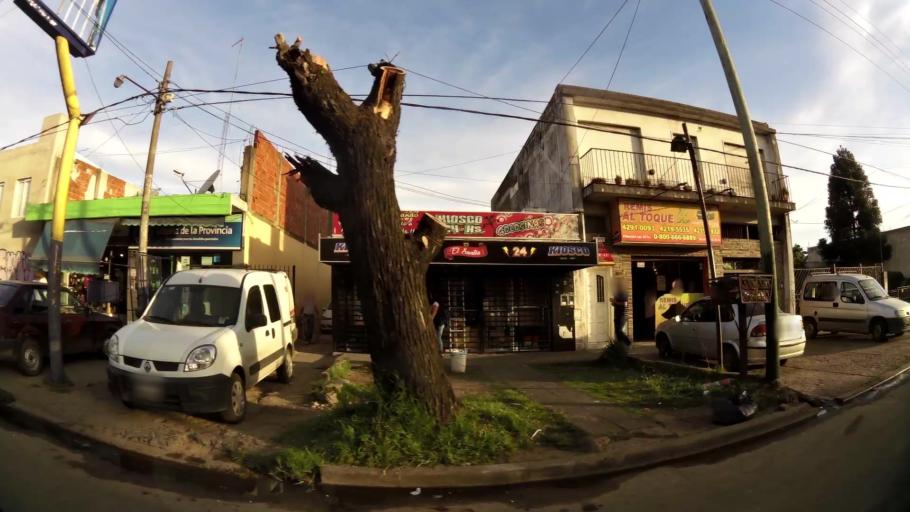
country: AR
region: Buenos Aires
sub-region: Partido de Almirante Brown
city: Adrogue
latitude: -34.7932
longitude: -58.3598
